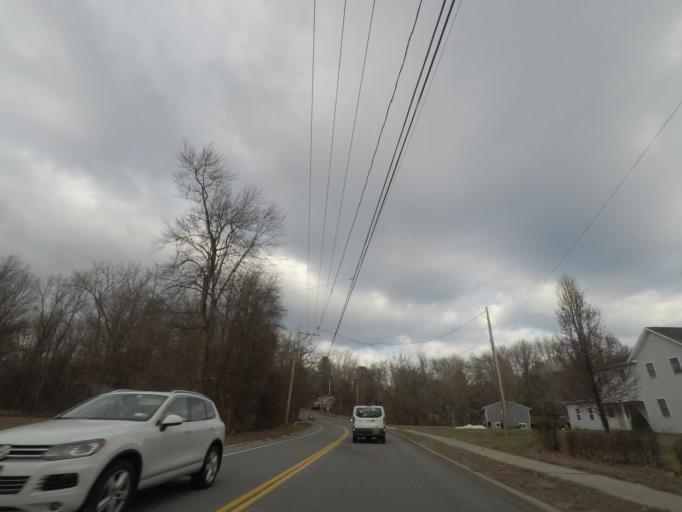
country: US
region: New York
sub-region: Albany County
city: Westmere
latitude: 42.6796
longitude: -73.8726
